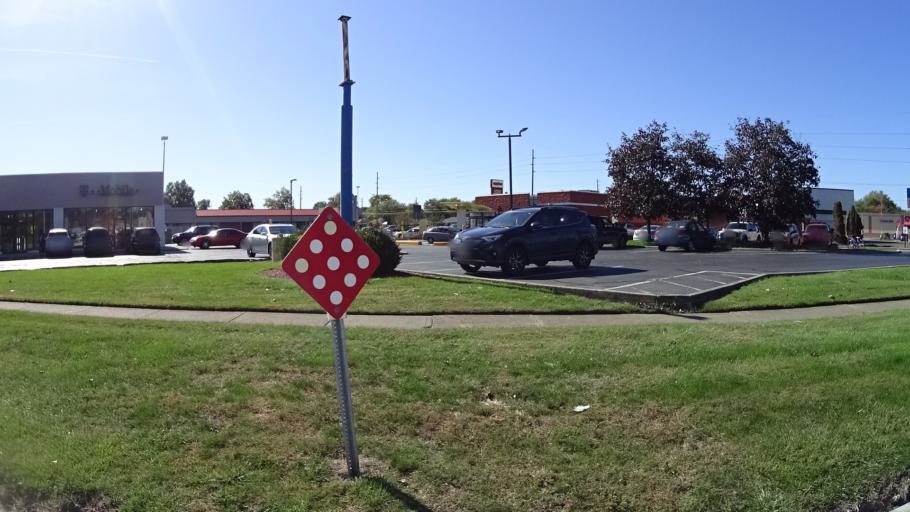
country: US
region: Ohio
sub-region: Lorain County
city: Lorain
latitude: 41.4412
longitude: -82.1841
